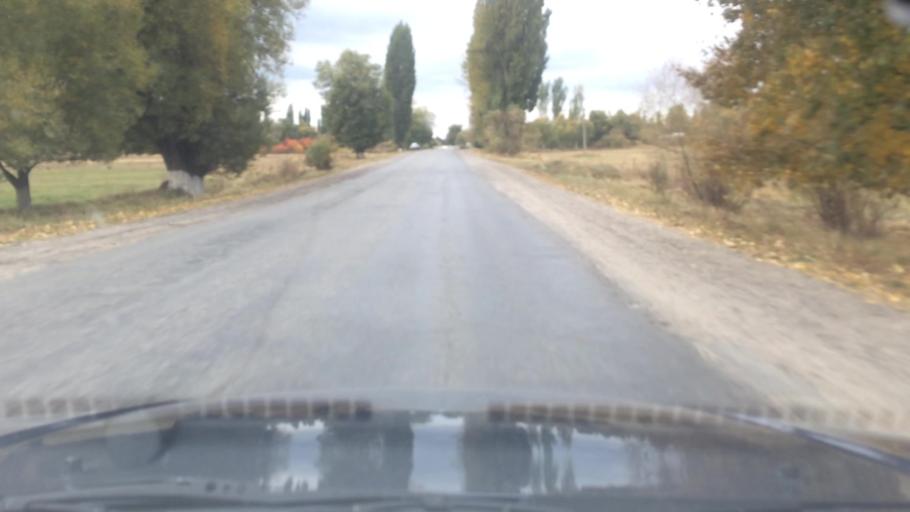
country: KG
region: Ysyk-Koel
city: Tyup
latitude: 42.7711
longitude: 78.1925
